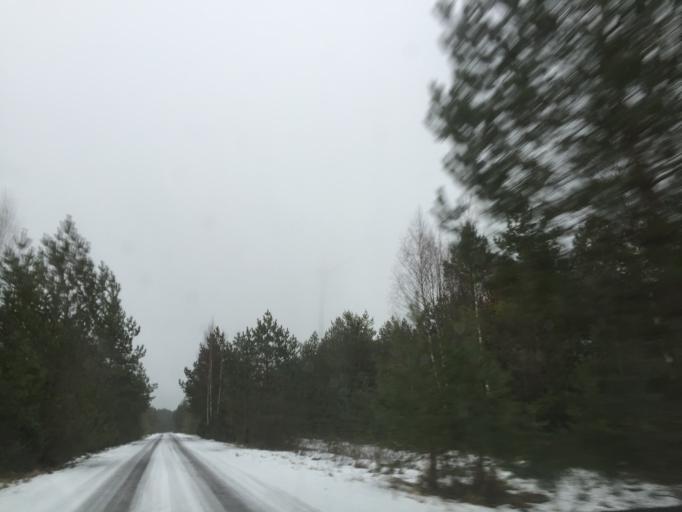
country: EE
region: Laeaene
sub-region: Lihula vald
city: Lihula
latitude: 58.6215
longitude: 23.5466
